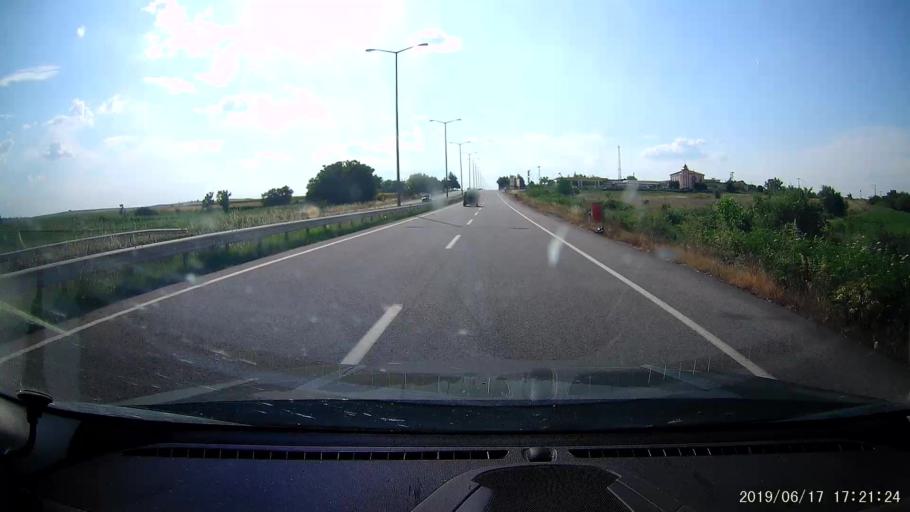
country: GR
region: East Macedonia and Thrace
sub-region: Nomos Evrou
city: Rizia
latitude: 41.7059
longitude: 26.3948
